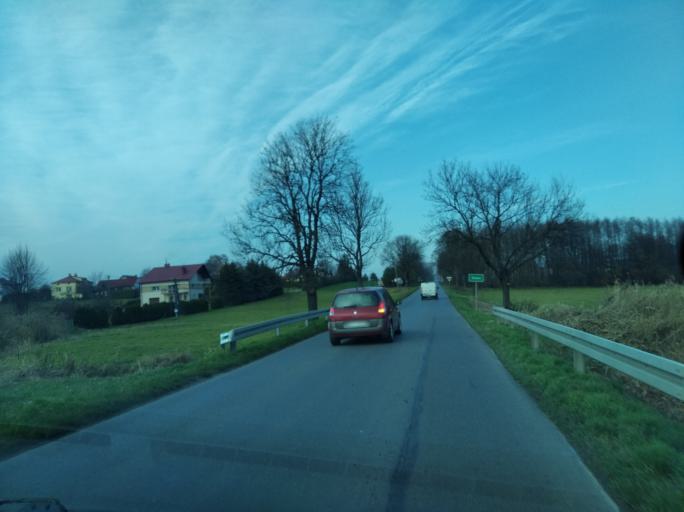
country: PL
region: Subcarpathian Voivodeship
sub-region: Powiat ropczycko-sedziszowski
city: Iwierzyce
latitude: 50.0449
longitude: 21.7452
